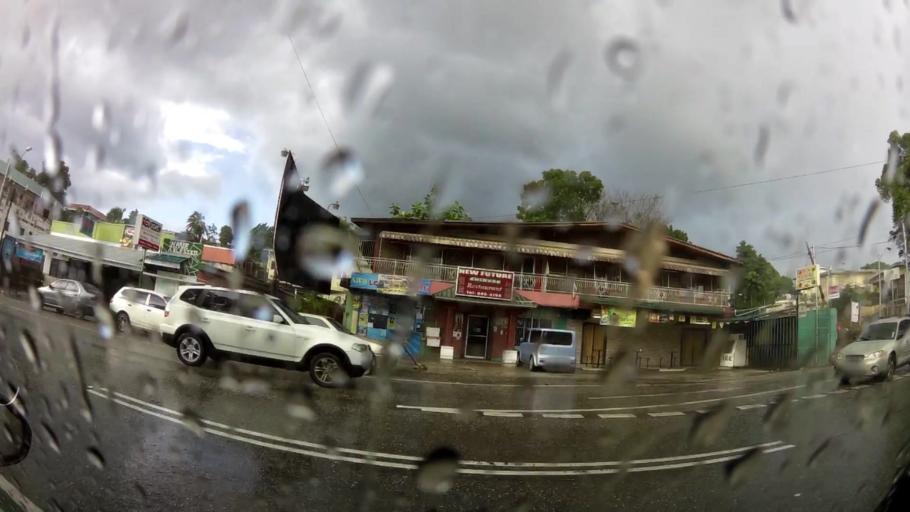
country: TT
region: Tunapuna/Piarco
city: Tunapuna
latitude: 10.6524
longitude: -61.4184
